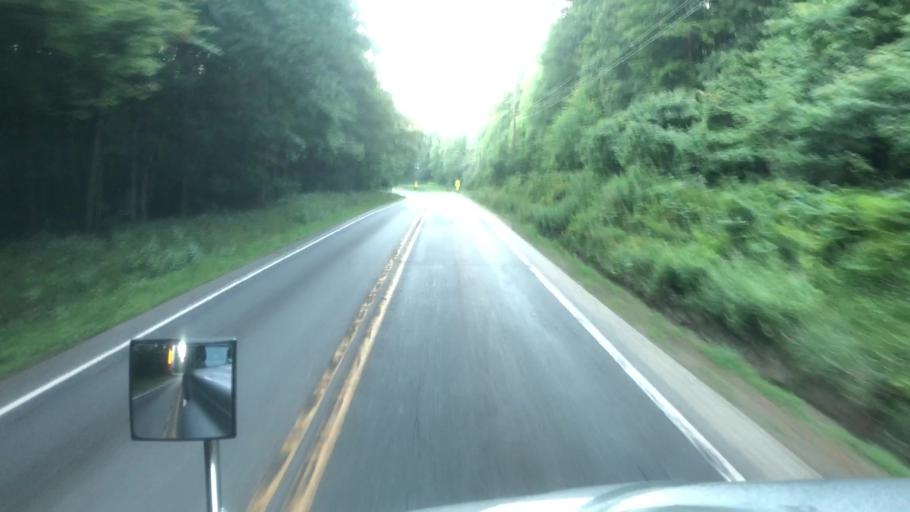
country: US
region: Pennsylvania
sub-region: Venango County
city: Hasson Heights
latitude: 41.5099
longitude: -79.6243
